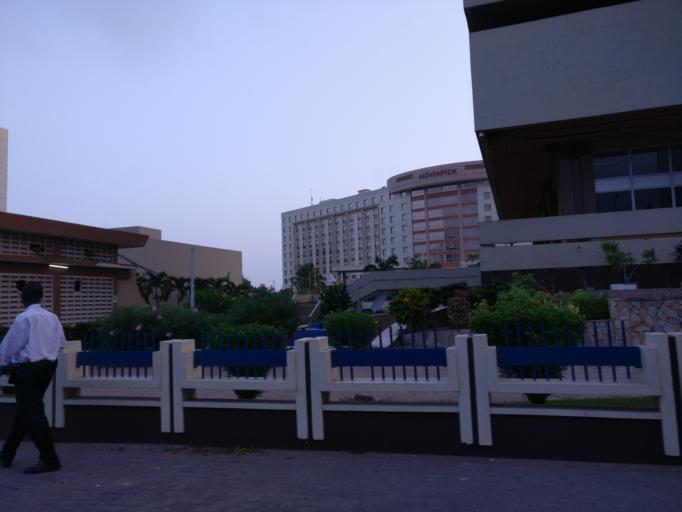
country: GH
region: Greater Accra
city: Accra
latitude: 5.5557
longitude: -0.2018
